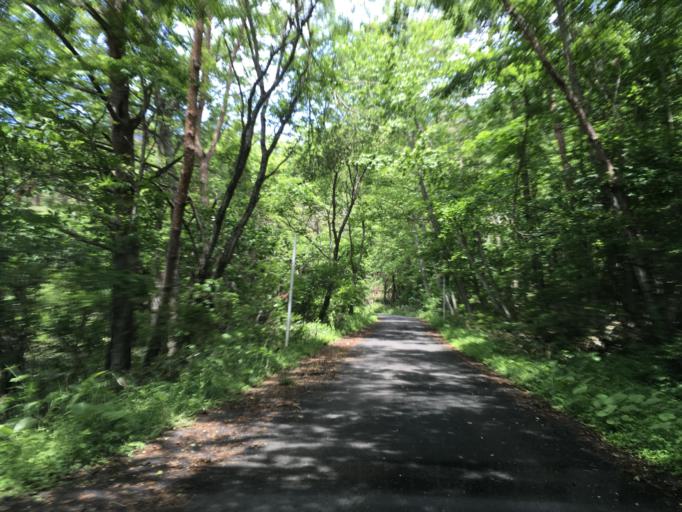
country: JP
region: Iwate
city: Mizusawa
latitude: 39.1281
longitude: 141.2957
